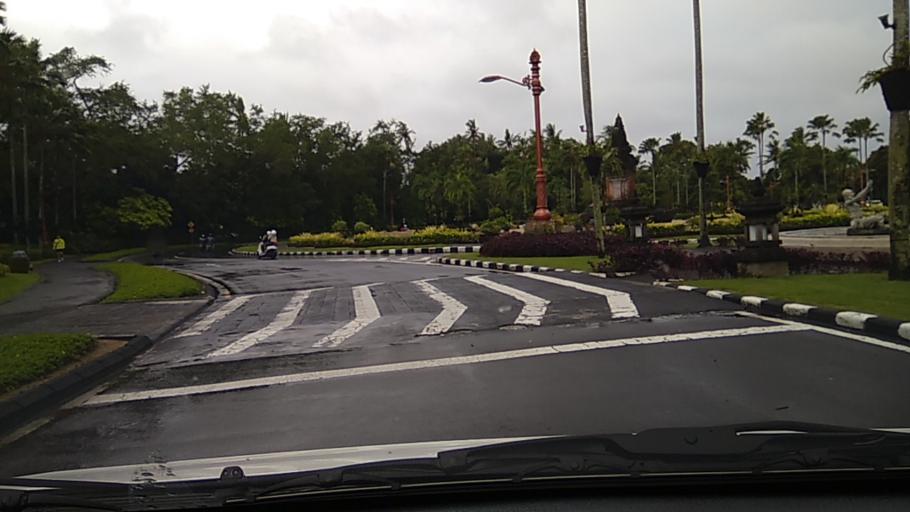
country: ID
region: Bali
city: Bualu
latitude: -8.7959
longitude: 115.2275
